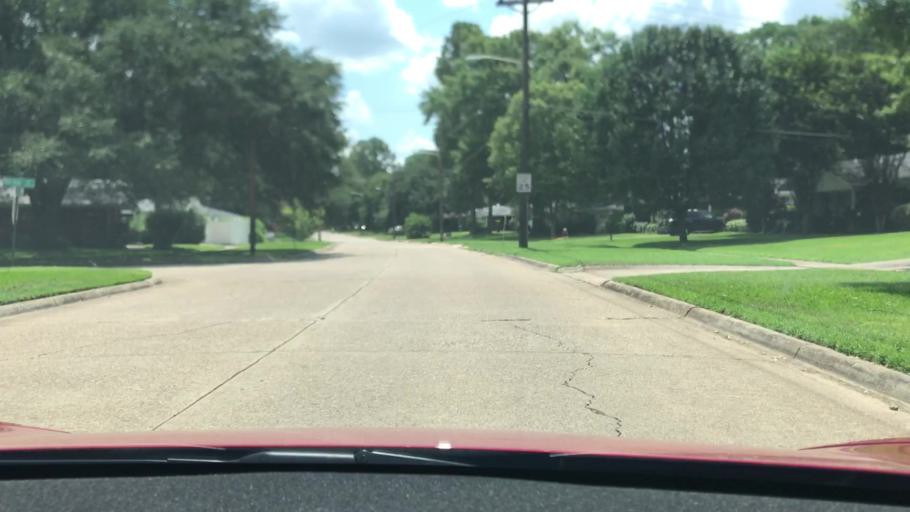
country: US
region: Louisiana
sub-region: Bossier Parish
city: Bossier City
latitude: 32.4580
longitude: -93.7322
